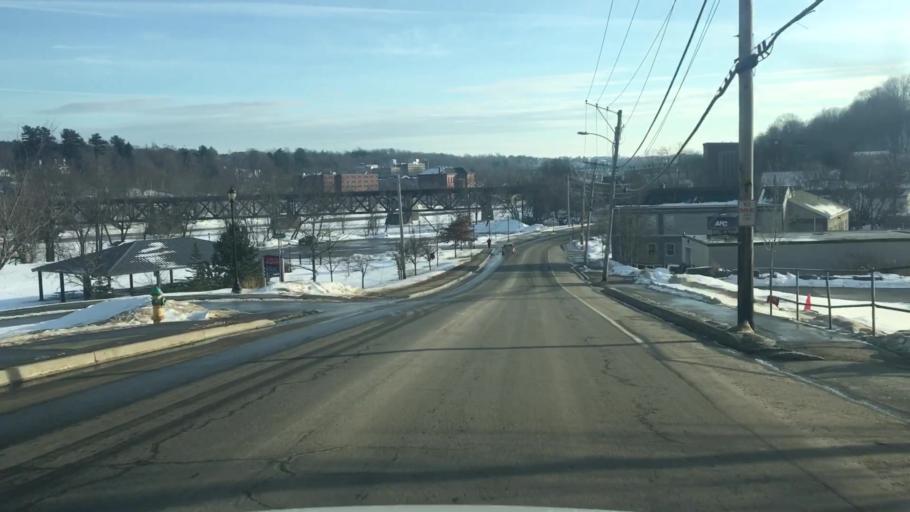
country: US
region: Maine
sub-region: Kennebec County
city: Augusta
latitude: 44.3224
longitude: -69.7736
